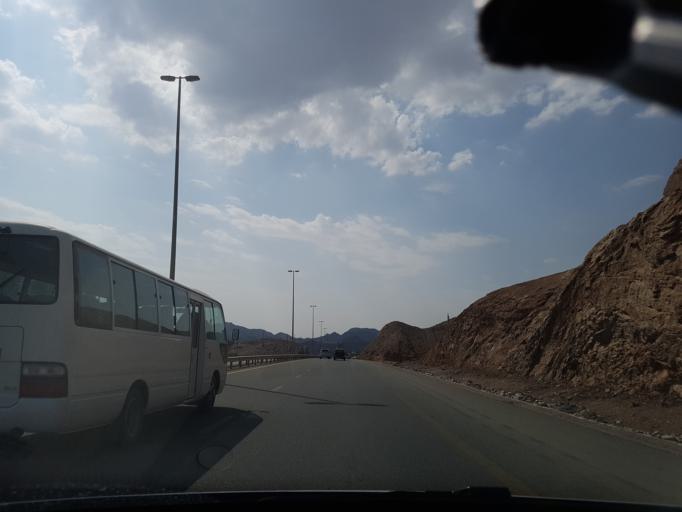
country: AE
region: Al Fujayrah
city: Dibba Al-Fujairah
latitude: 25.5157
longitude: 56.0837
